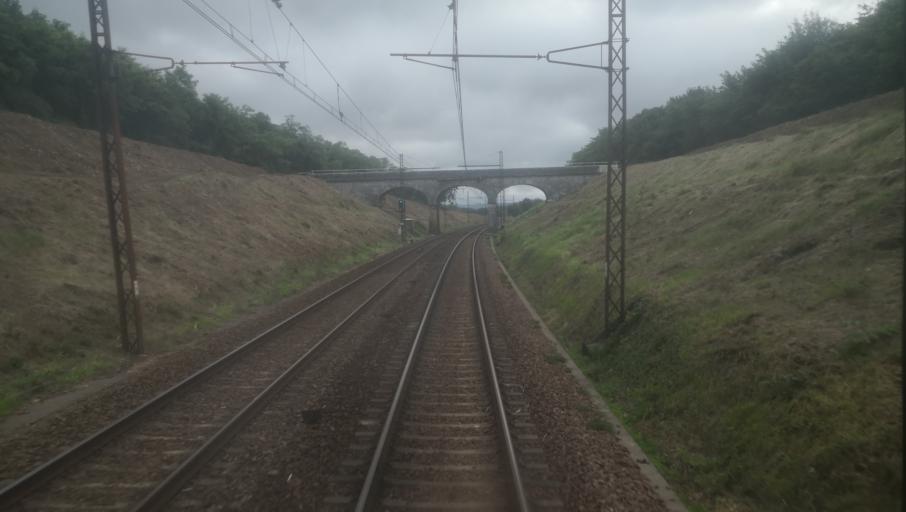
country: FR
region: Centre
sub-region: Departement du Cher
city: Vierzon
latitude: 47.1891
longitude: 2.0715
